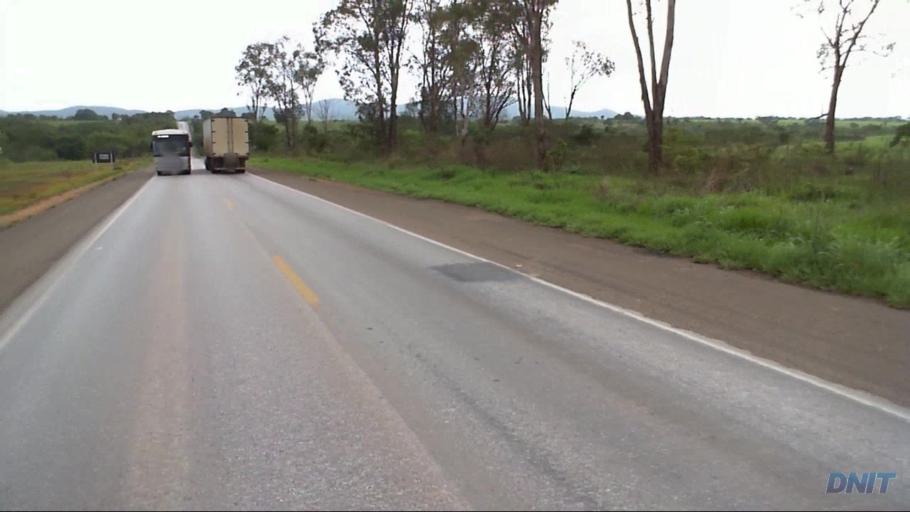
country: BR
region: Goias
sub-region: Uruacu
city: Uruacu
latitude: -14.6175
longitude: -49.1703
